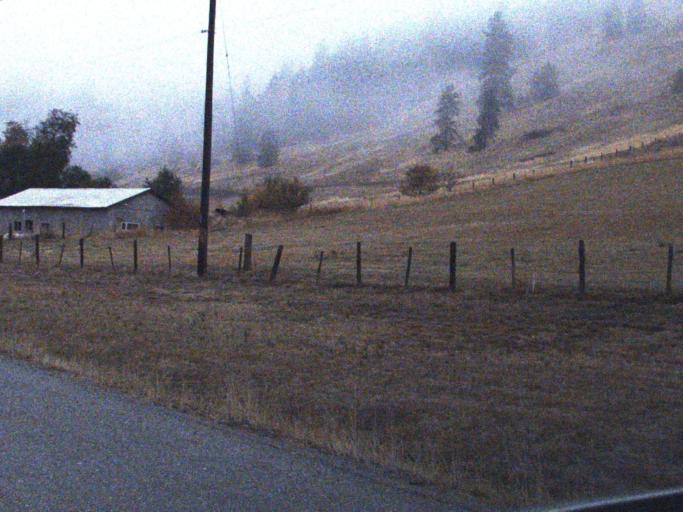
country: US
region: Washington
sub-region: Stevens County
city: Kettle Falls
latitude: 48.6115
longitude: -118.0409
